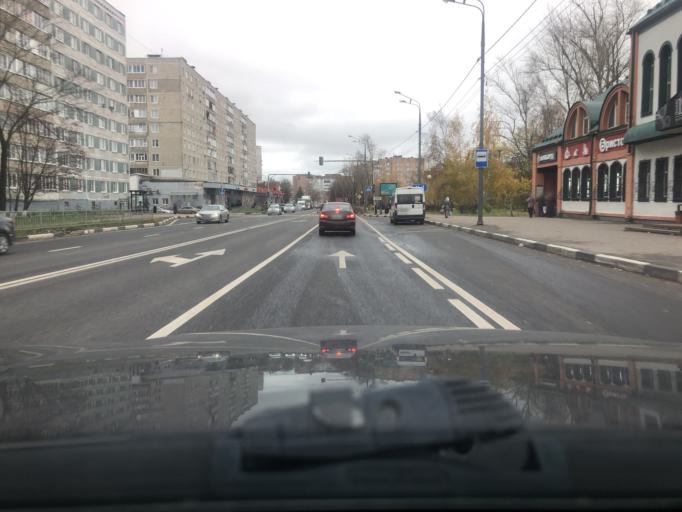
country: RU
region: Moskovskaya
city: Sergiyev Posad
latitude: 56.3302
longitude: 38.1316
